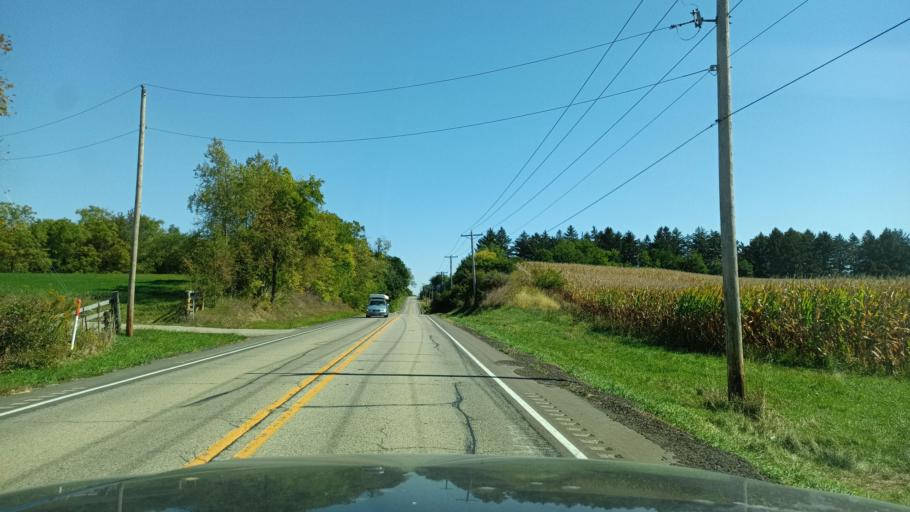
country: US
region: Illinois
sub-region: McLean County
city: Danvers
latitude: 40.6169
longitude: -89.2270
